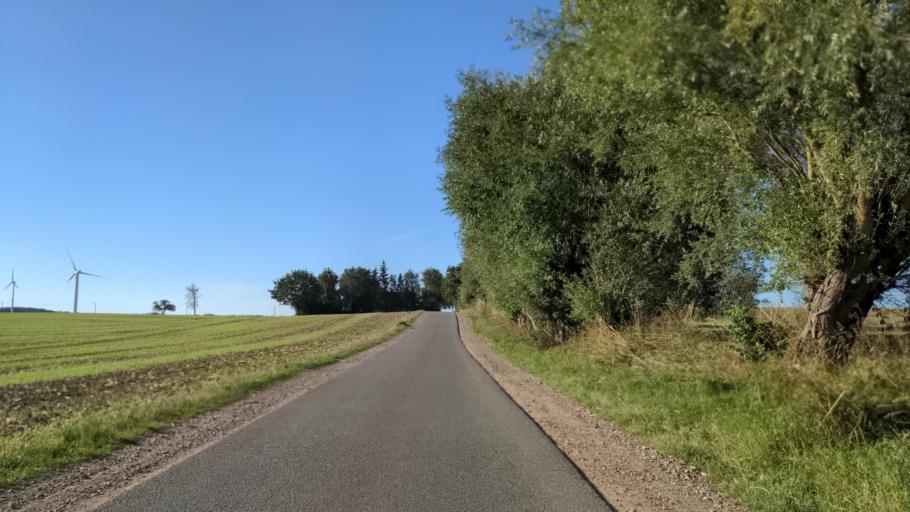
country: DE
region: Mecklenburg-Vorpommern
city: Kalkhorst
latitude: 53.9560
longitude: 11.0099
